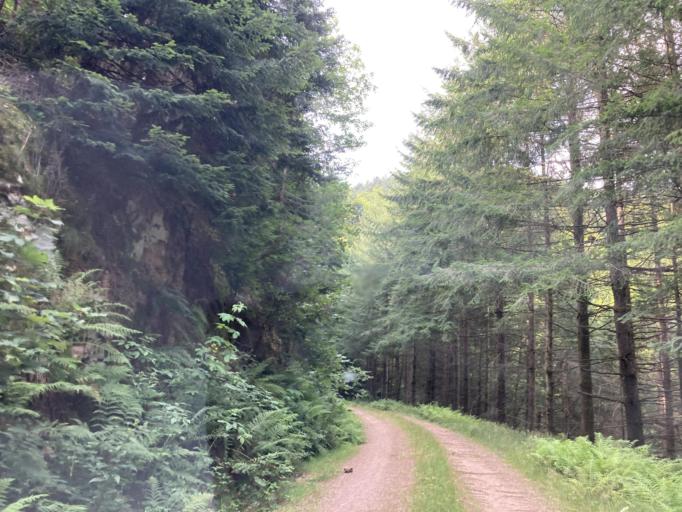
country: DE
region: Baden-Wuerttemberg
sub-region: Freiburg Region
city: Schonach im Schwarzwald
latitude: 48.1632
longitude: 8.1529
